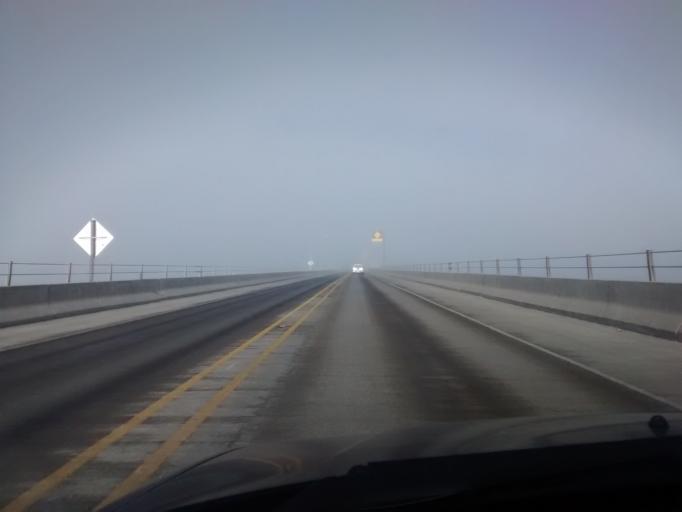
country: US
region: Washington
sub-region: Kitsap County
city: Lofall
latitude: 47.8547
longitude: -122.6153
